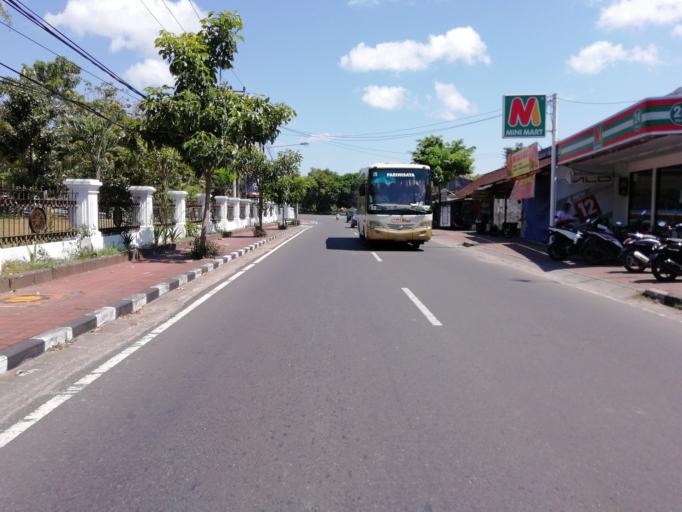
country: ID
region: Bali
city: Jimbaran
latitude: -8.7978
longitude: 115.1722
